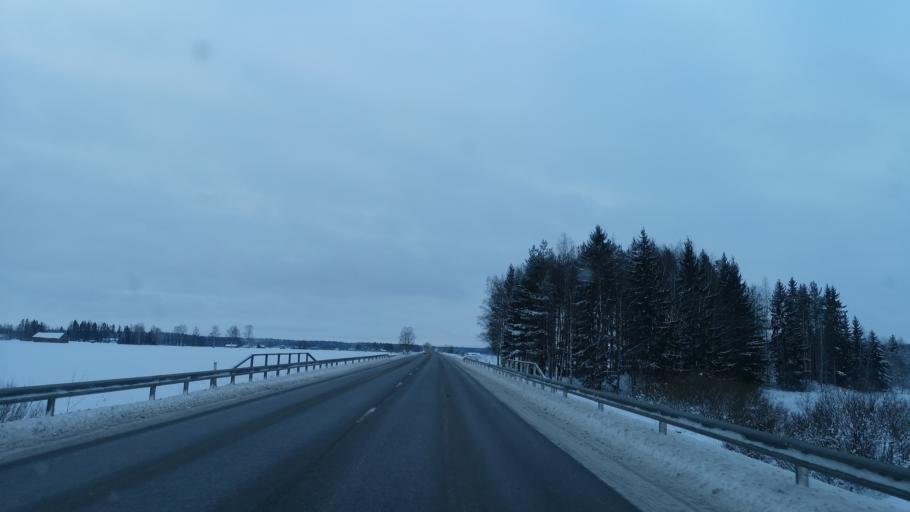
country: FI
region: Varsinais-Suomi
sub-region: Loimaa
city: Loimaa
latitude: 60.8939
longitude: 23.1153
